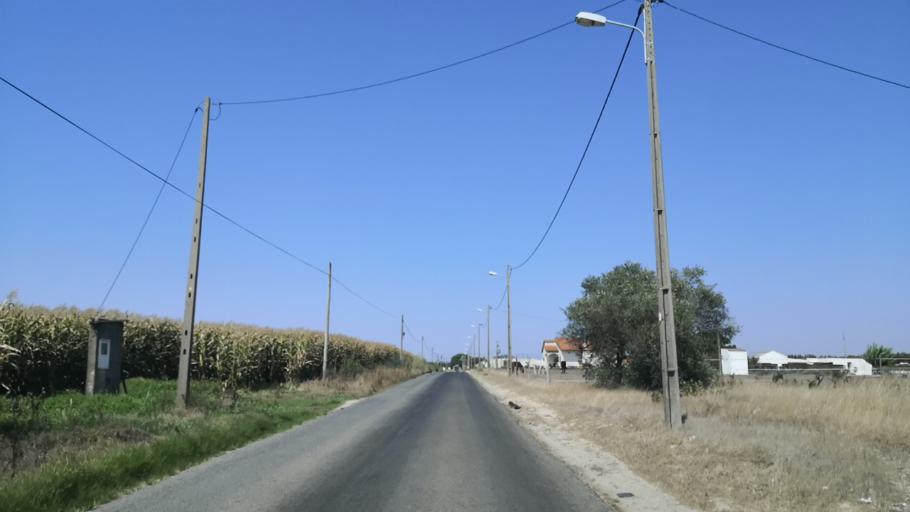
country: PT
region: Santarem
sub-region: Benavente
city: Poceirao
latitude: 38.7075
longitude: -8.7188
